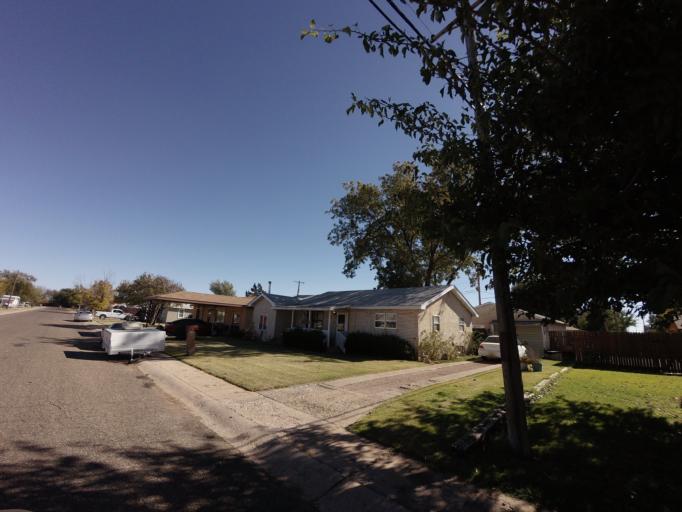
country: US
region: New Mexico
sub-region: Curry County
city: Clovis
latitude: 34.4294
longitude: -103.2053
